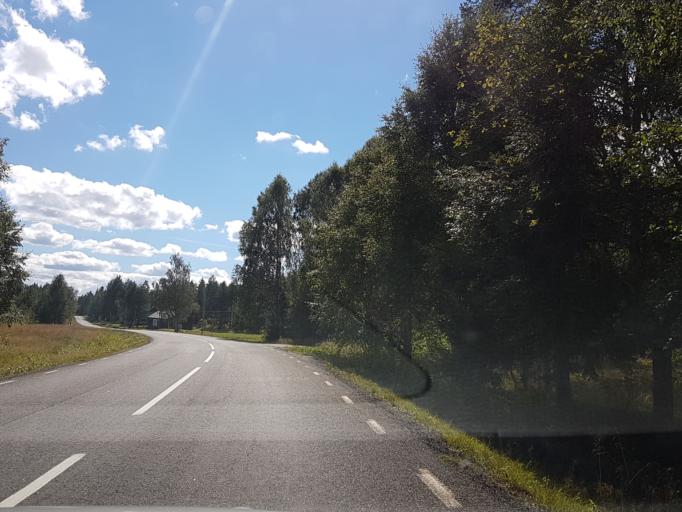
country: SE
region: Vaesterbotten
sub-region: Umea Kommun
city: Saevar
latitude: 64.1251
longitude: 20.5418
